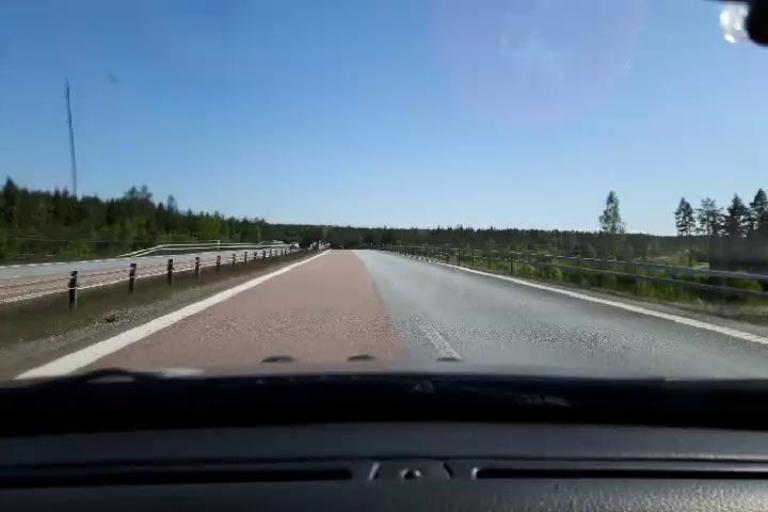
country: SE
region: Gaevleborg
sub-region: Soderhamns Kommun
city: Soderhamn
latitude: 61.3362
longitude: 17.0169
